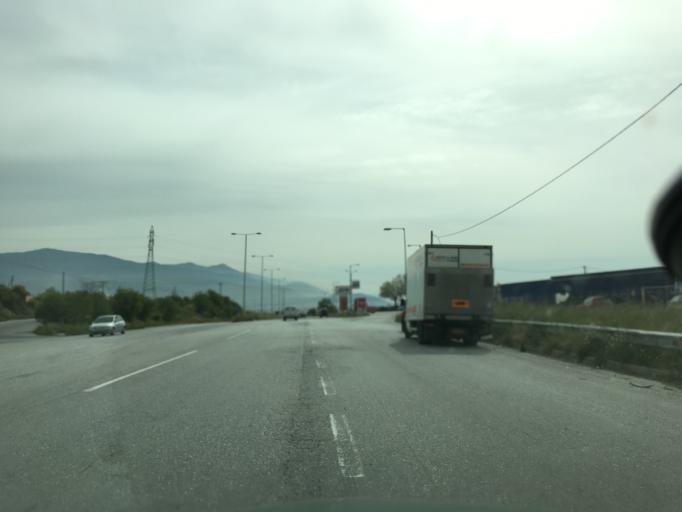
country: GR
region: Thessaly
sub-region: Nomos Magnisias
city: Nea Ionia
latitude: 39.3803
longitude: 22.8661
